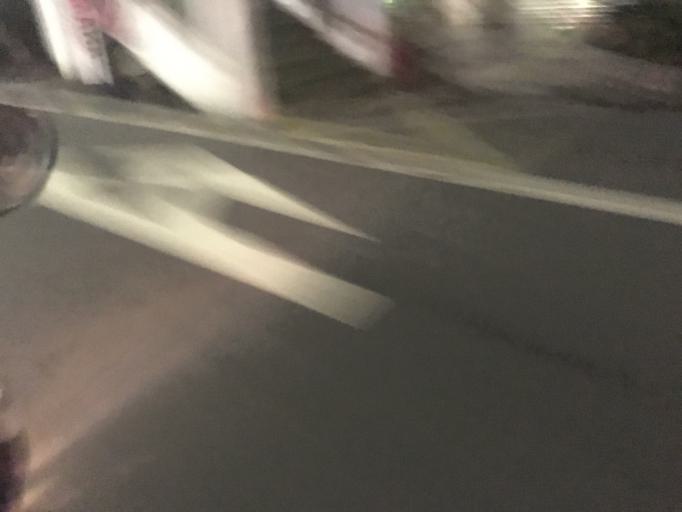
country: TW
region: Taiwan
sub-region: Hsinchu
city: Hsinchu
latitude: 24.8094
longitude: 120.9604
